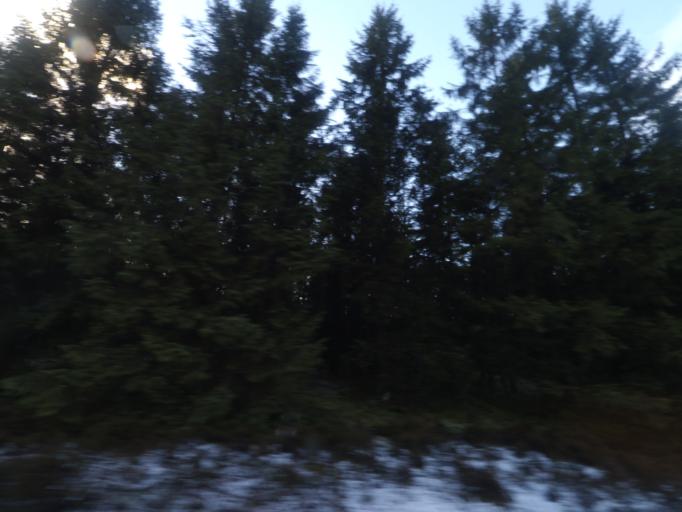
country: DK
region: Central Jutland
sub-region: Ikast-Brande Kommune
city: Brande
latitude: 56.0126
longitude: 9.1638
